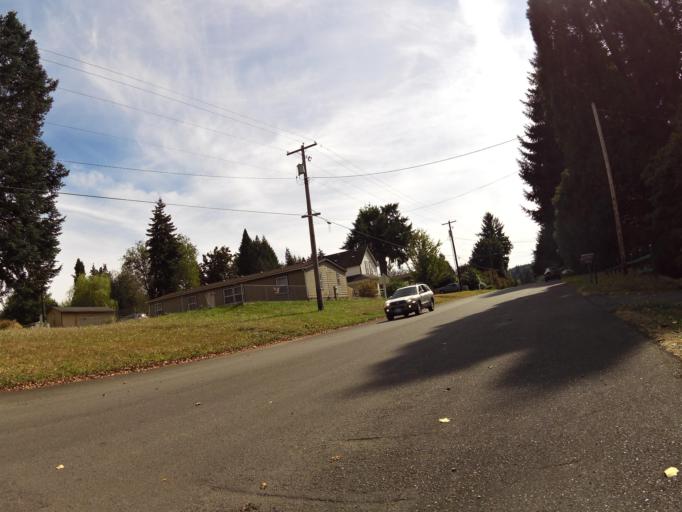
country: US
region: Washington
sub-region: Lewis County
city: Winlock
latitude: 46.4008
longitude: -122.9563
